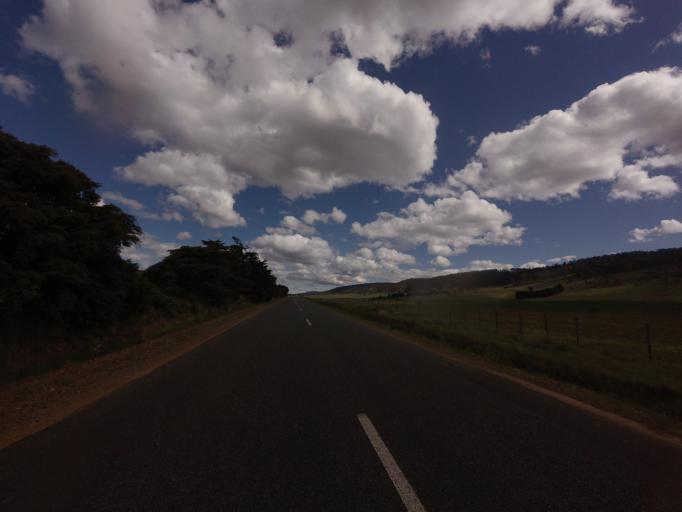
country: AU
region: Tasmania
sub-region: Brighton
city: Bridgewater
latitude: -42.4072
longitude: 147.3104
